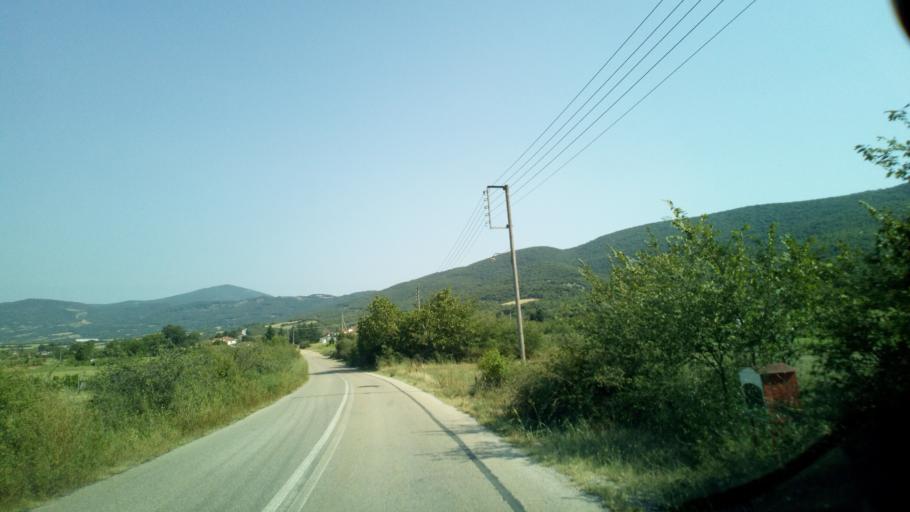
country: GR
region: Central Macedonia
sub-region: Nomos Chalkidikis
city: Galatista
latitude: 40.5106
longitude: 23.3696
